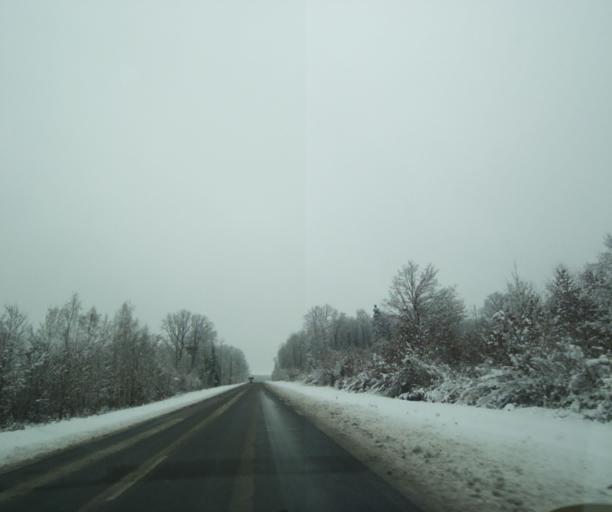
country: FR
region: Champagne-Ardenne
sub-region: Departement de la Haute-Marne
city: Laneuville-a-Remy
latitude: 48.5506
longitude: 4.8353
